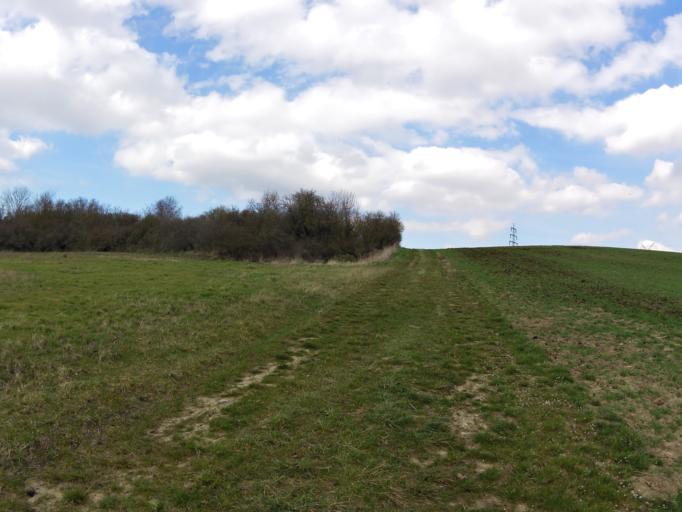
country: DE
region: Bavaria
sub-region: Regierungsbezirk Unterfranken
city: Biebelried
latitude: 49.7441
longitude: 10.0956
